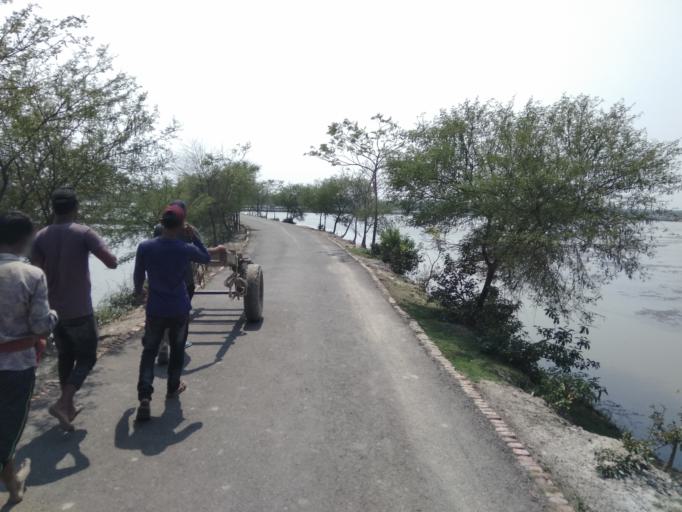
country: IN
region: West Bengal
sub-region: North 24 Parganas
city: Taki
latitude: 22.4000
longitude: 89.2138
